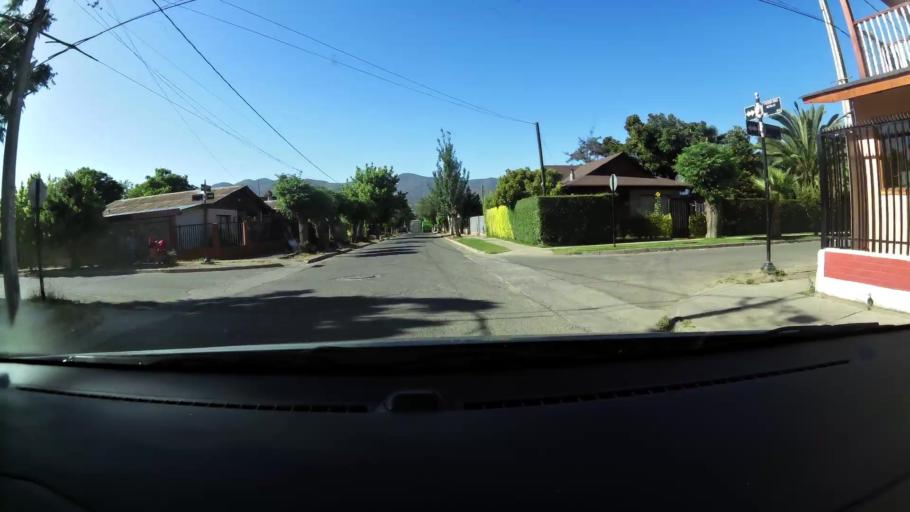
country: CL
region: Santiago Metropolitan
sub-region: Provincia de Chacabuco
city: Lampa
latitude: -33.3935
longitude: -71.1283
